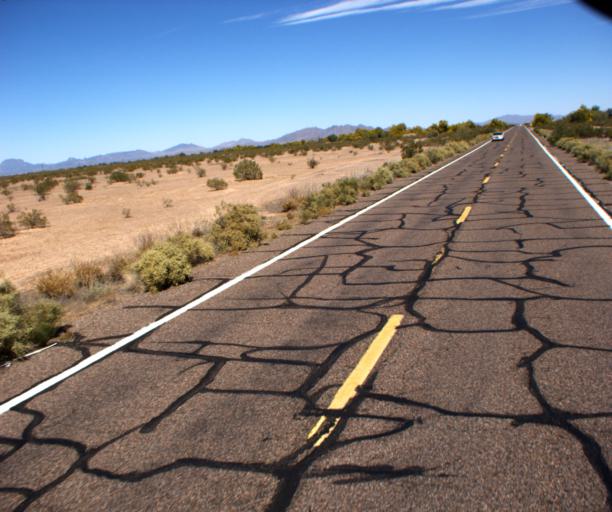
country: US
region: Arizona
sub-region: Maricopa County
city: Gila Bend
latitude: 32.8774
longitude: -112.7560
